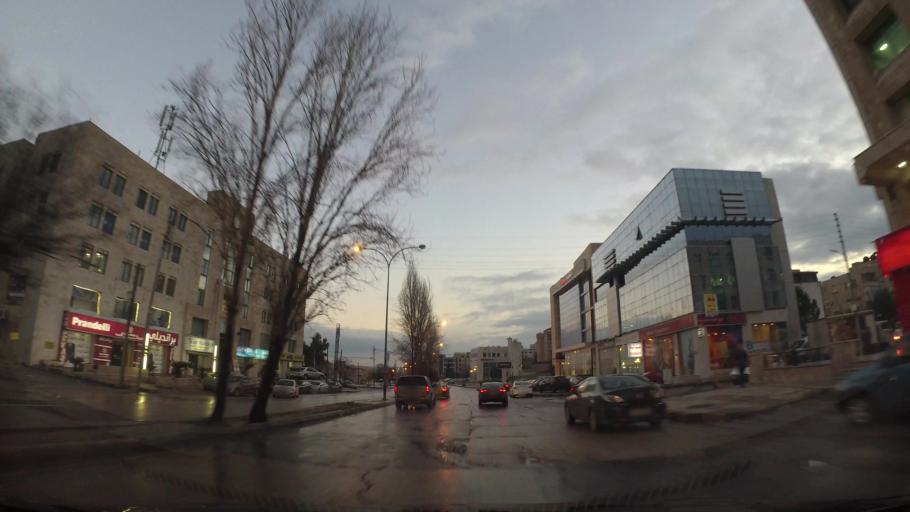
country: JO
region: Amman
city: Al Jubayhah
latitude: 31.9721
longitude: 35.8863
